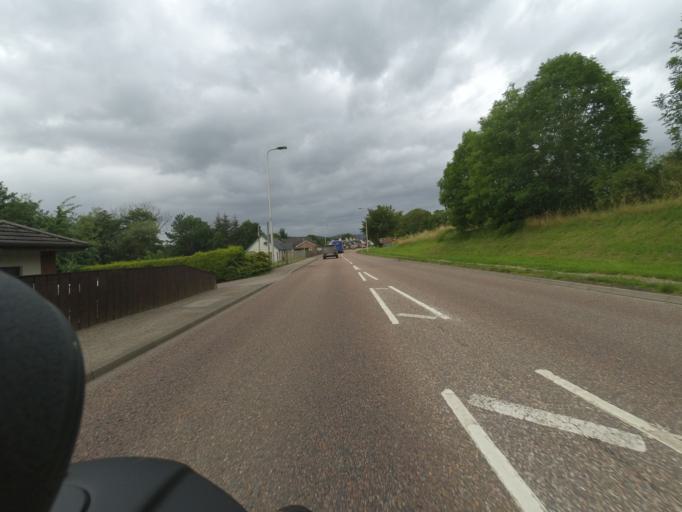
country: GB
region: Scotland
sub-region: Highland
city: Muir of Ord
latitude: 57.5645
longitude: -4.5773
